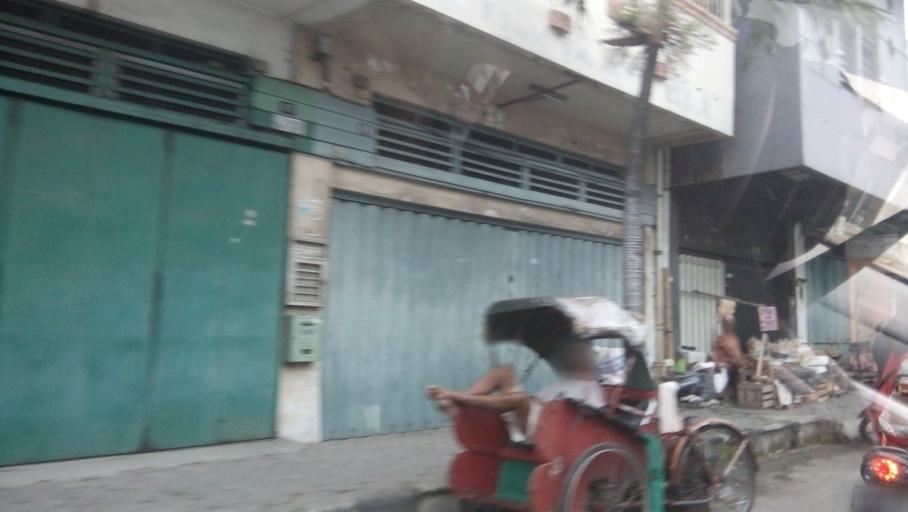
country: ID
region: Central Java
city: Surakarta
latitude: -7.5743
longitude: 110.8226
